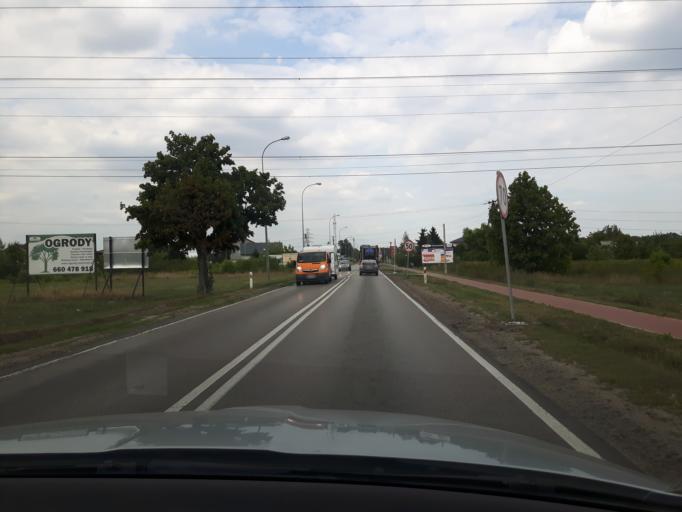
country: PL
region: Masovian Voivodeship
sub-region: Powiat legionowski
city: Stanislawow Pierwszy
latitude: 52.3711
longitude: 21.0289
